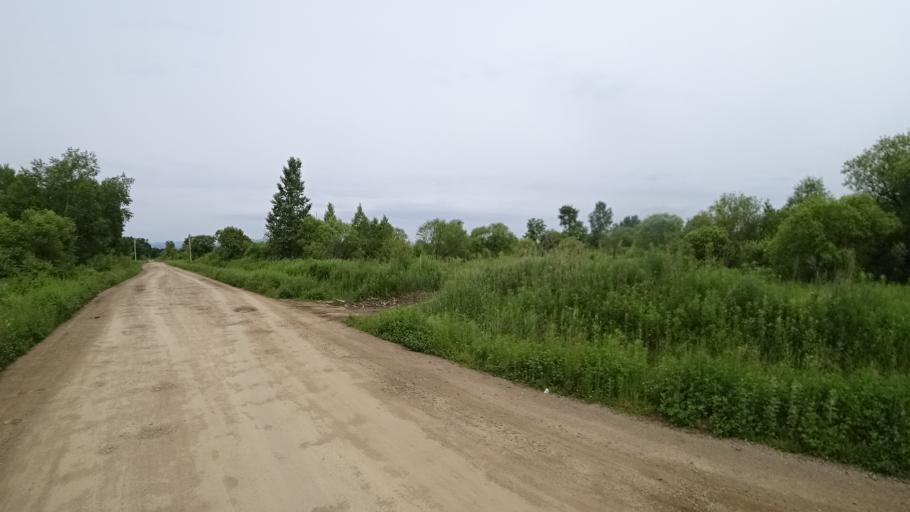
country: RU
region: Primorskiy
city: Arsen'yev
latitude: 44.1943
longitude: 133.3094
